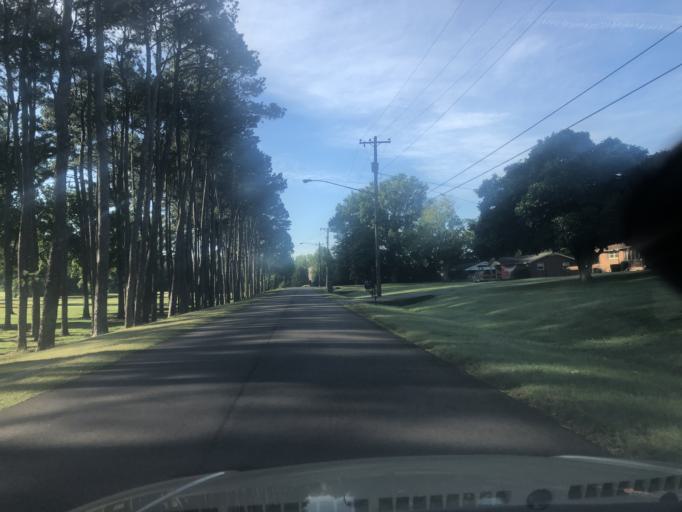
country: US
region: Tennessee
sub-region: Davidson County
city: Lakewood
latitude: 36.2468
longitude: -86.6503
